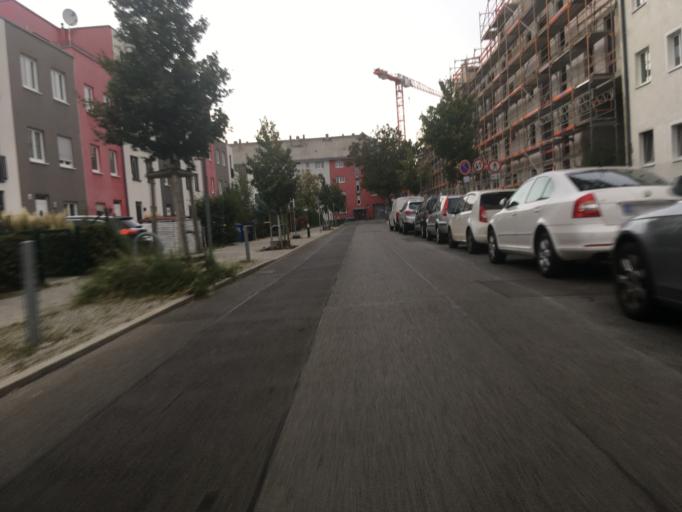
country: DE
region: Berlin
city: Fennpfuhl
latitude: 52.5383
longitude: 13.4841
